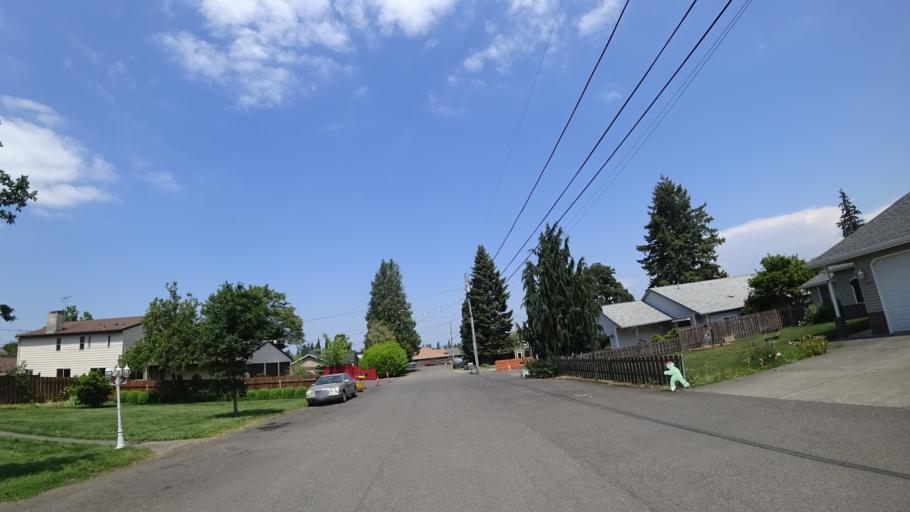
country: US
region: Oregon
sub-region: Multnomah County
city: Fairview
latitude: 45.5364
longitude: -122.5038
